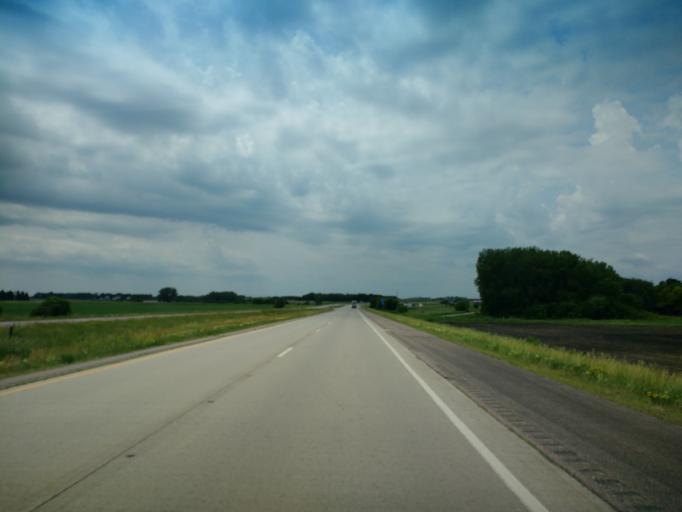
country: US
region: Minnesota
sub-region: Cottonwood County
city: Mountain Lake
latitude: 43.9546
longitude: -94.7882
